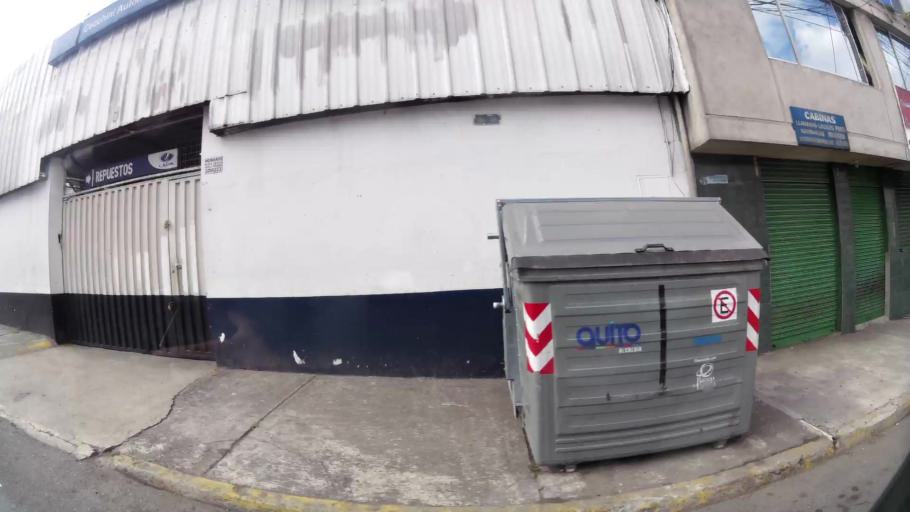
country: EC
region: Pichincha
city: Quito
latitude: -0.1531
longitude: -78.4660
